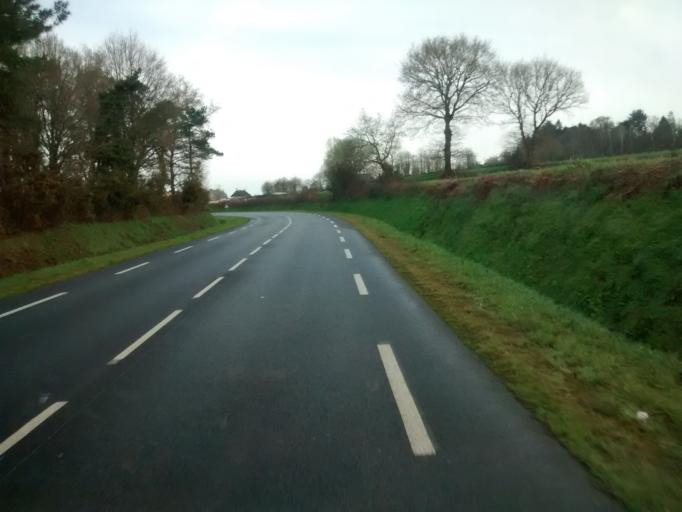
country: FR
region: Brittany
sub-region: Departement du Morbihan
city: Malestroit
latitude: 47.8346
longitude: -2.3926
